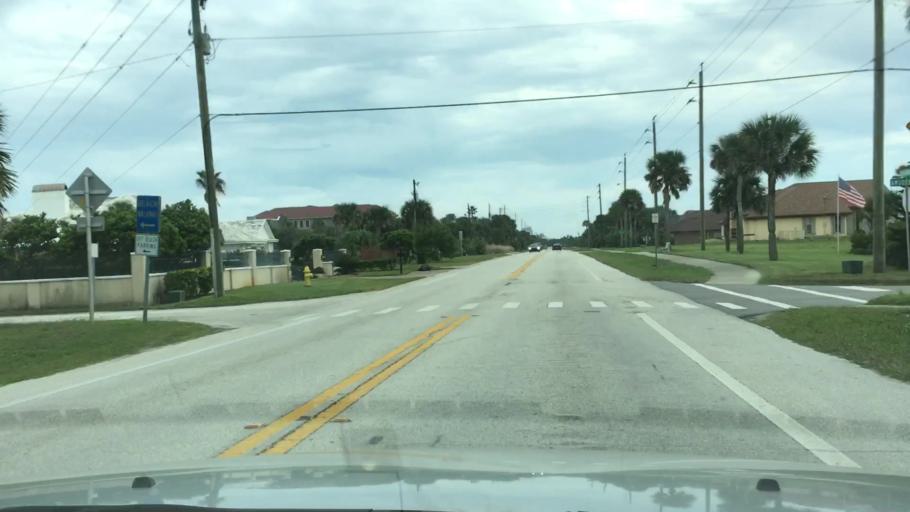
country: US
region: Florida
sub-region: Volusia County
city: Ormond Beach
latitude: 29.3077
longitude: -81.0477
